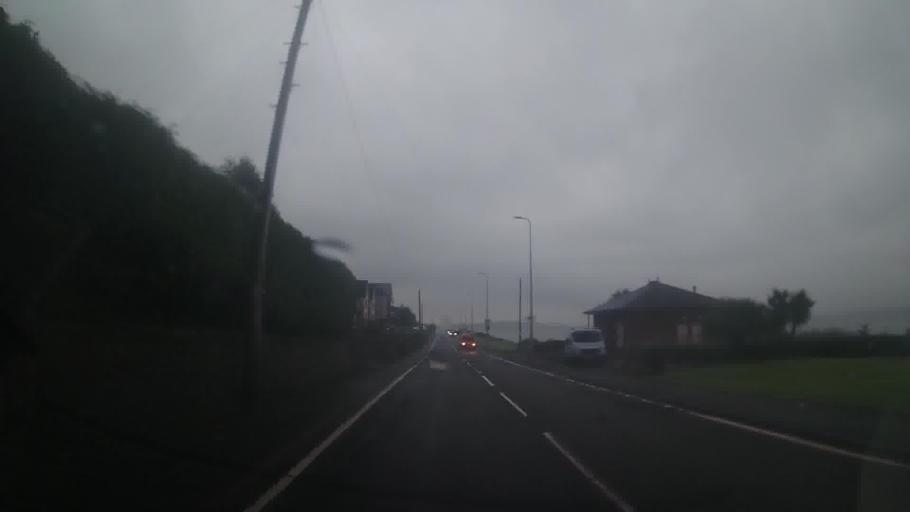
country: GB
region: Scotland
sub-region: North Ayrshire
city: Skelmorlie
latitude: 55.8661
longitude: -4.8914
